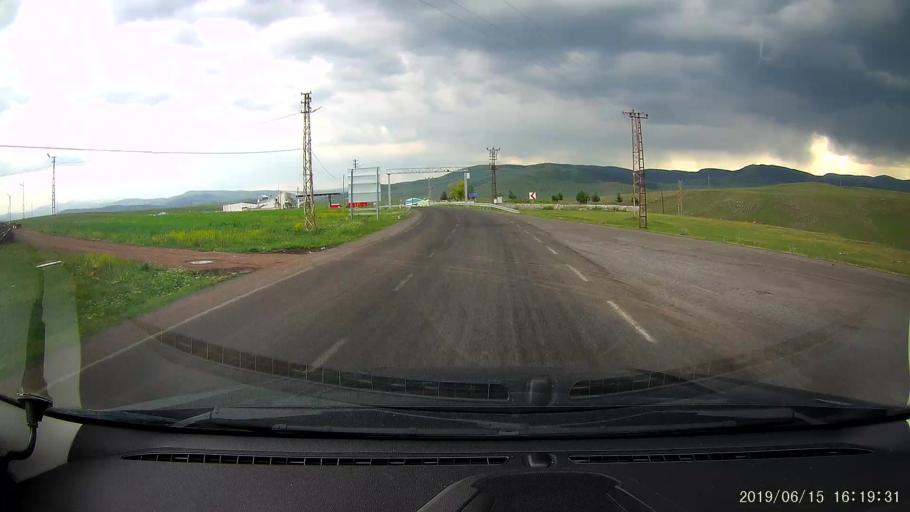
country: TR
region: Ardahan
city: Hanak
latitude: 41.2277
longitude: 42.8499
